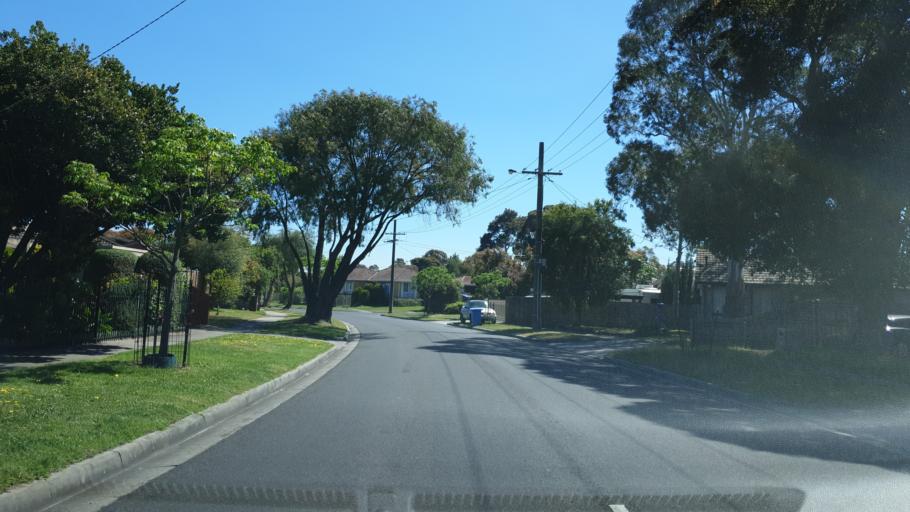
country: AU
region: Victoria
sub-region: Casey
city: Cranbourne
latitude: -38.1044
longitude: 145.2752
